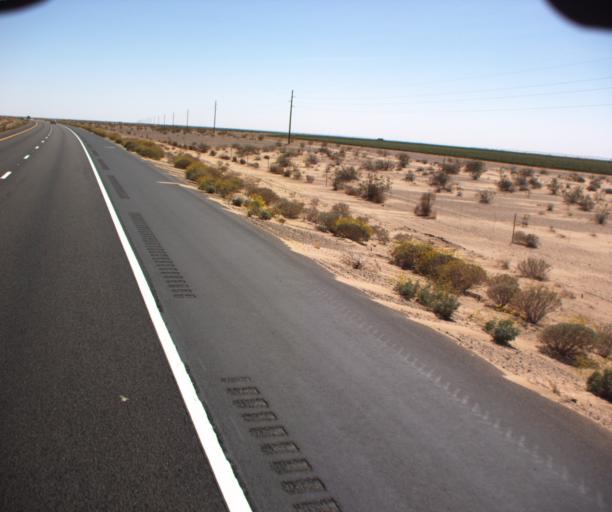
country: US
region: Arizona
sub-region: Yuma County
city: Somerton
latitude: 32.5192
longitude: -114.5620
